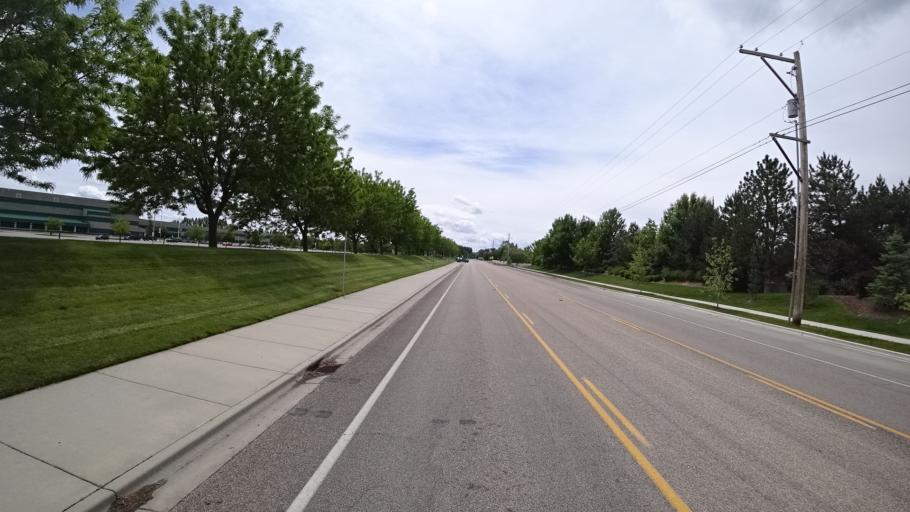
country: US
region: Idaho
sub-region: Ada County
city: Eagle
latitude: 43.7020
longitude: -116.4036
